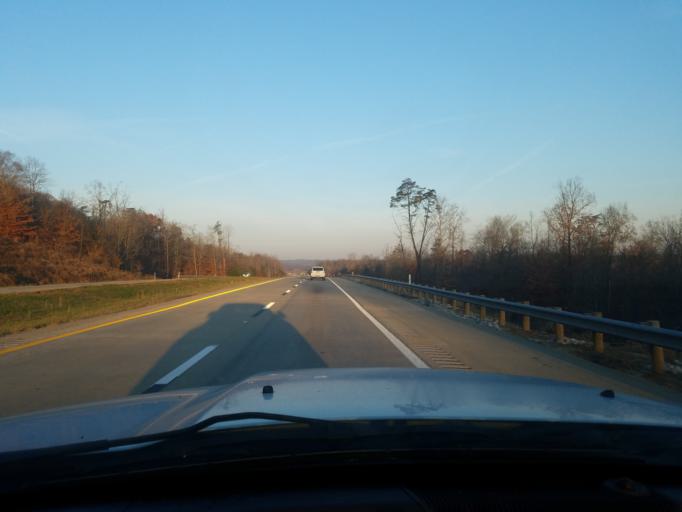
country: US
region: West Virginia
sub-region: Putnam County
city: Eleanor
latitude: 38.5357
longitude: -81.9573
